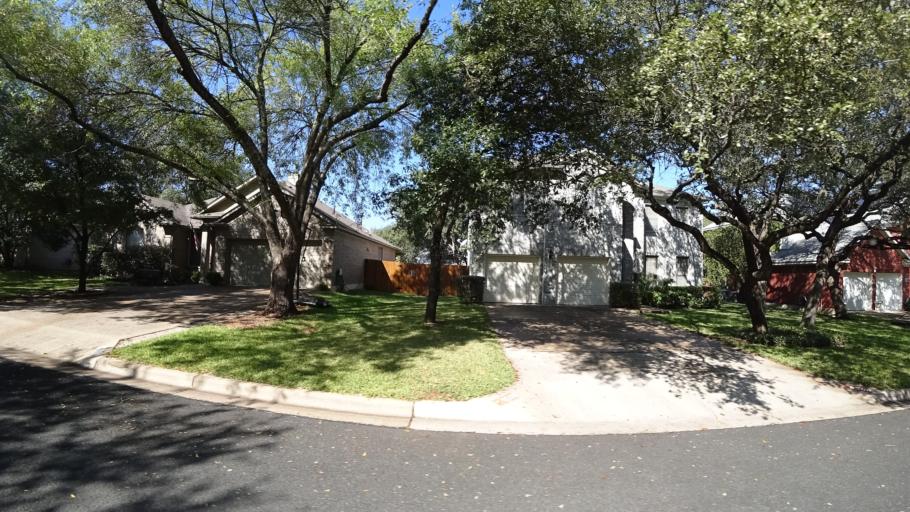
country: US
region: Texas
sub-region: Travis County
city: Shady Hollow
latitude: 30.2116
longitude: -97.8677
